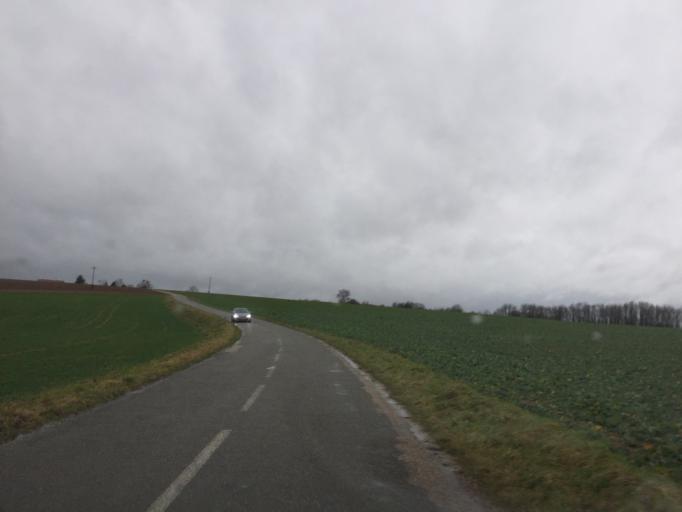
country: FR
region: Franche-Comte
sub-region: Departement du Jura
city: Dole
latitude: 47.1581
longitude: 5.5074
